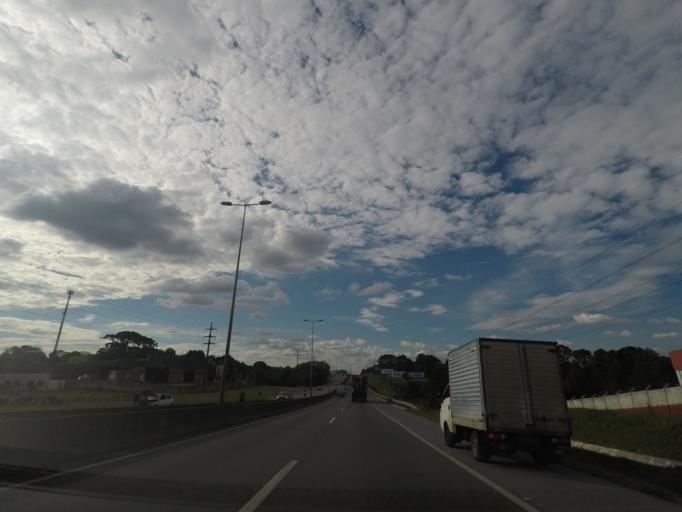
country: BR
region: Parana
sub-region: Araucaria
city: Araucaria
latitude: -25.5901
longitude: -49.3151
